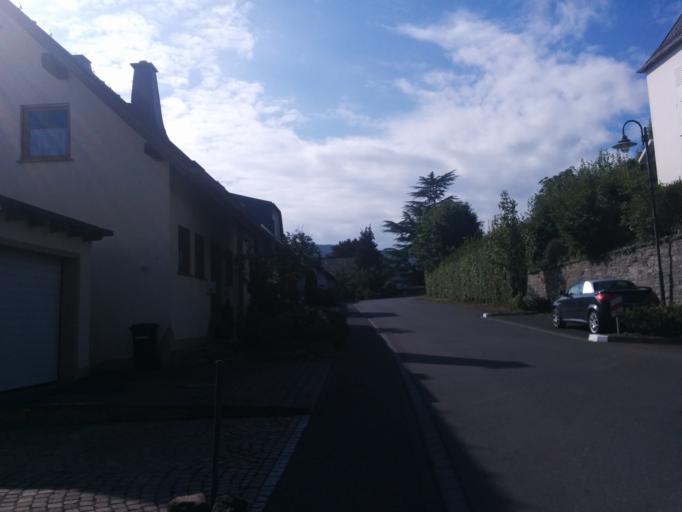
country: DE
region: Rheinland-Pfalz
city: Bernkastel-Kues
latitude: 49.9193
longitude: 7.0629
